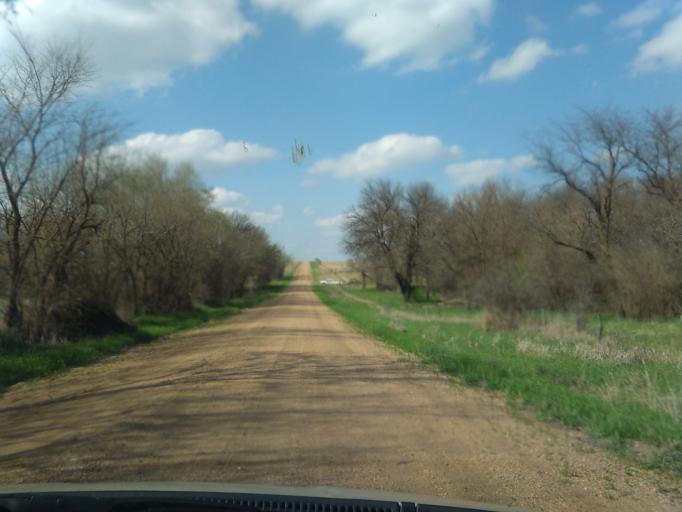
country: US
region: Nebraska
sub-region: Webster County
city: Red Cloud
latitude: 40.0085
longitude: -98.3491
